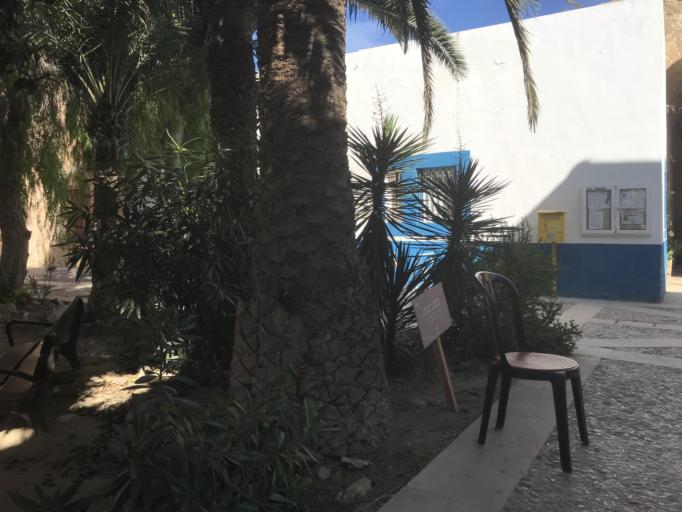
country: ES
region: Valencia
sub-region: Provincia de Alicante
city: Santa Pola
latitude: 38.1663
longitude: -0.4805
